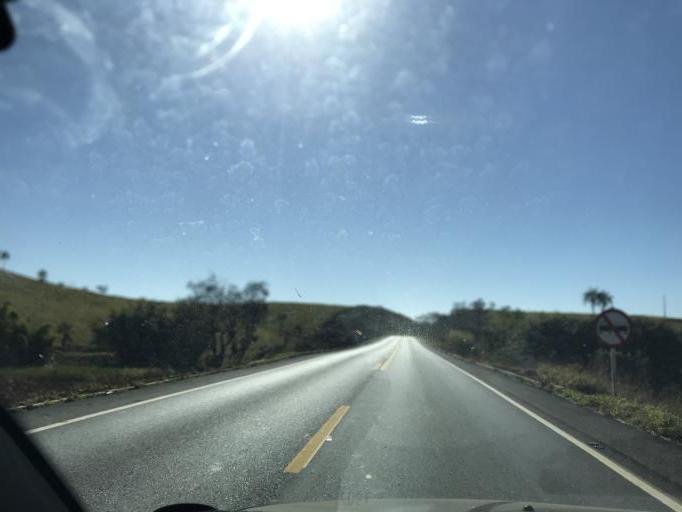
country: BR
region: Minas Gerais
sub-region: Bambui
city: Bambui
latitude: -19.8482
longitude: -45.9981
